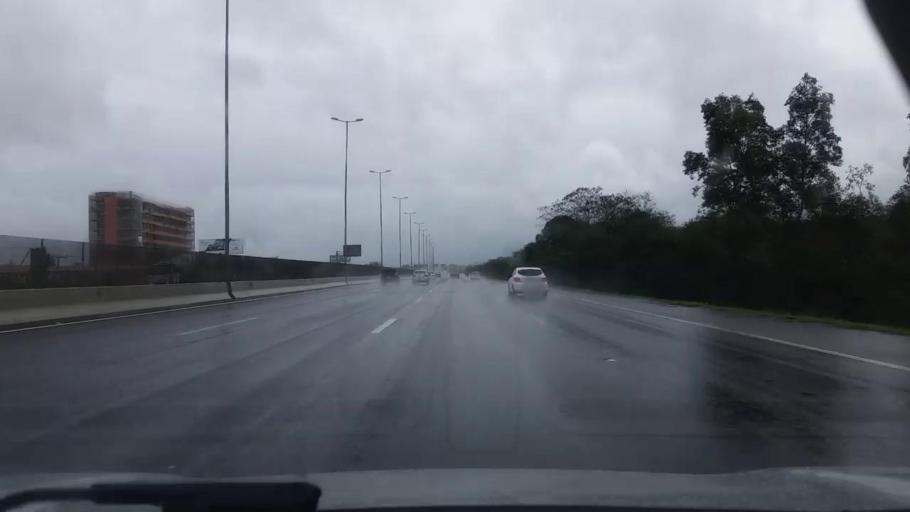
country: BR
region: Rio Grande do Sul
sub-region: Canoas
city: Canoas
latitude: -29.9680
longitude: -51.1566
